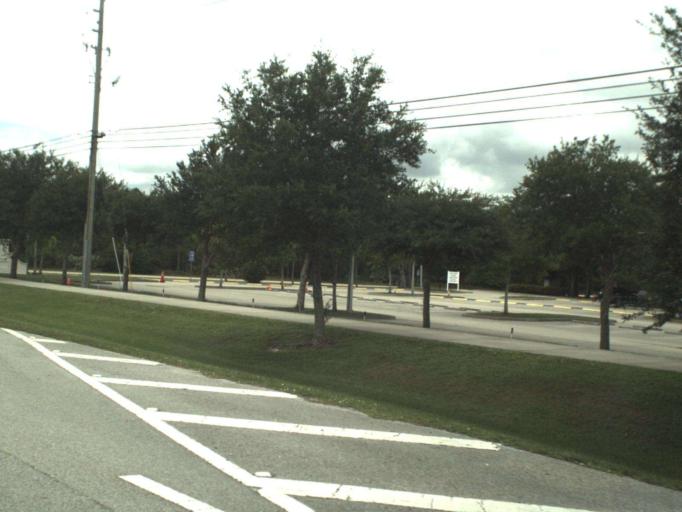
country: US
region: Florida
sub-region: Saint Lucie County
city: White City
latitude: 27.3614
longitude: -80.3571
